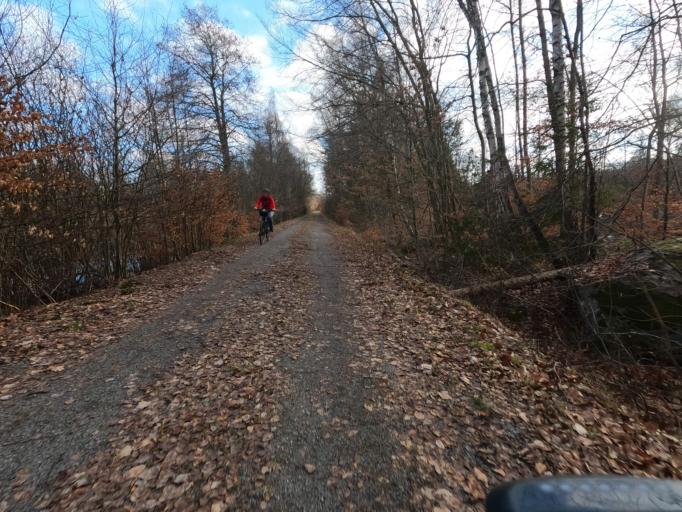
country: SE
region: Kronoberg
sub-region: Vaxjo Kommun
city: Gemla
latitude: 56.6655
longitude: 14.6211
